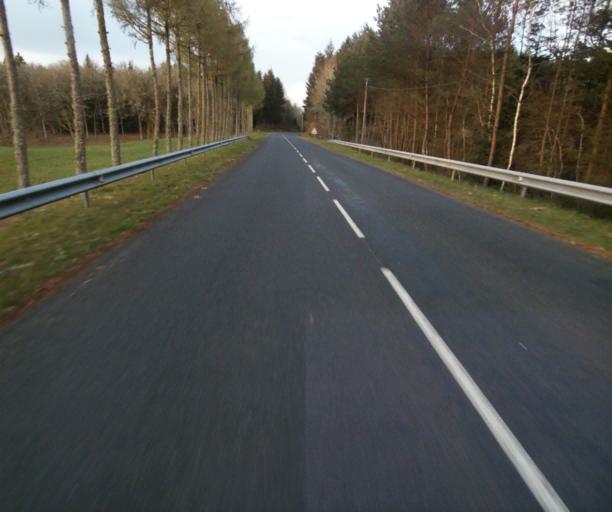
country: FR
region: Limousin
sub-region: Departement de la Correze
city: Correze
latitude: 45.2785
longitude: 1.9569
